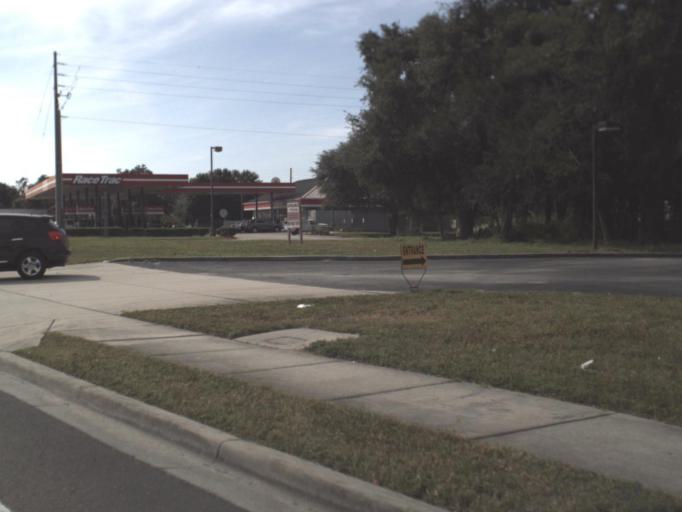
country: US
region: Florida
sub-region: Orange County
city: Holden Heights
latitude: 28.5069
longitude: -81.4178
